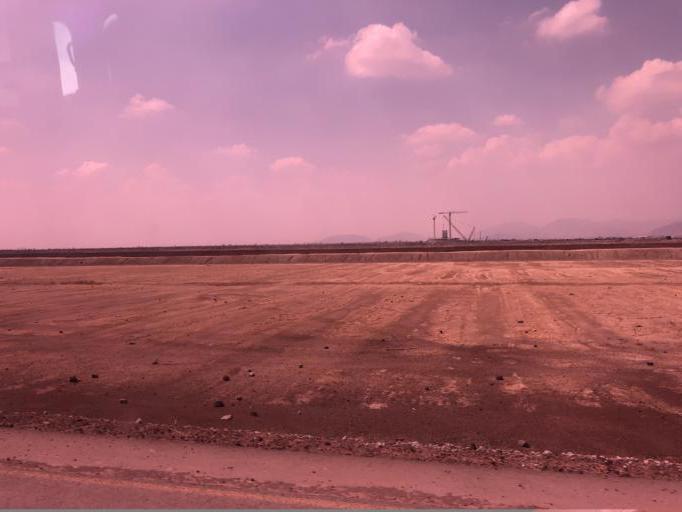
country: MX
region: Mexico
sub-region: Atenco
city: Colonia el Salado
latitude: 19.5227
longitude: -98.9857
